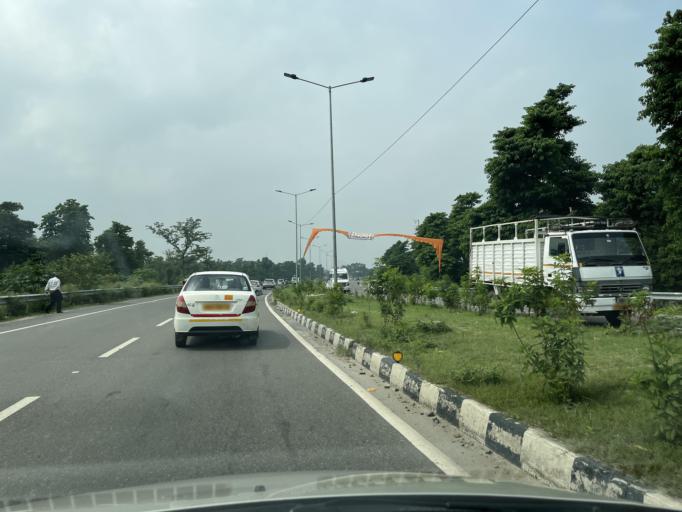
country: IN
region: Uttarakhand
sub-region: Haridwar
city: Haridwar
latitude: 29.9656
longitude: 78.1795
